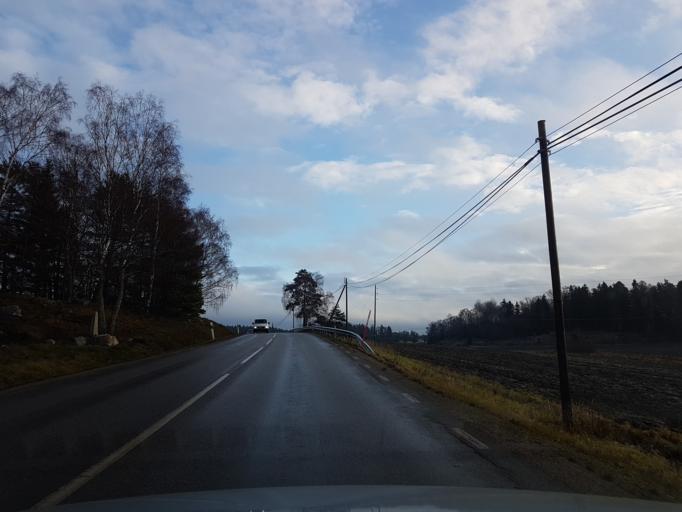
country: SE
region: Stockholm
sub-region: Nykvarns Kommun
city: Nykvarn
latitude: 59.2035
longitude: 17.4107
